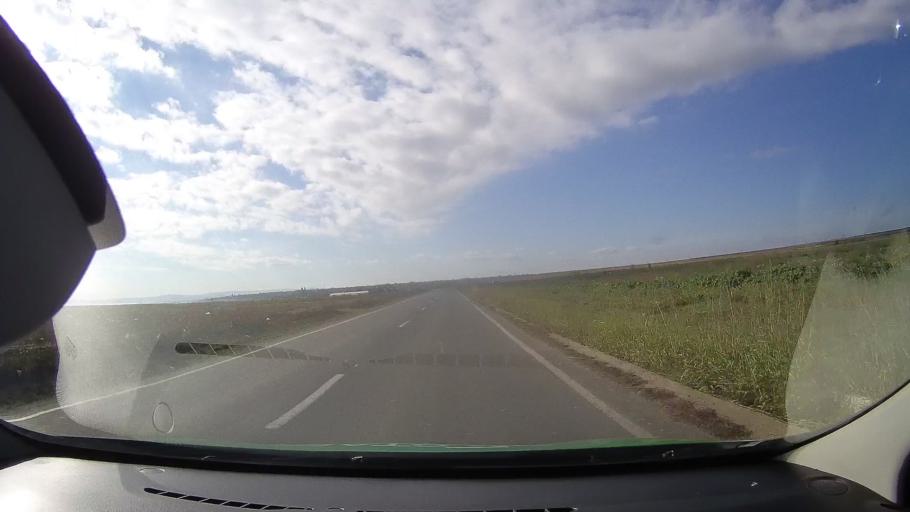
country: RO
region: Tulcea
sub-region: Comuna Sarichioi
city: Sarichioi
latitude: 44.9671
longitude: 28.8665
